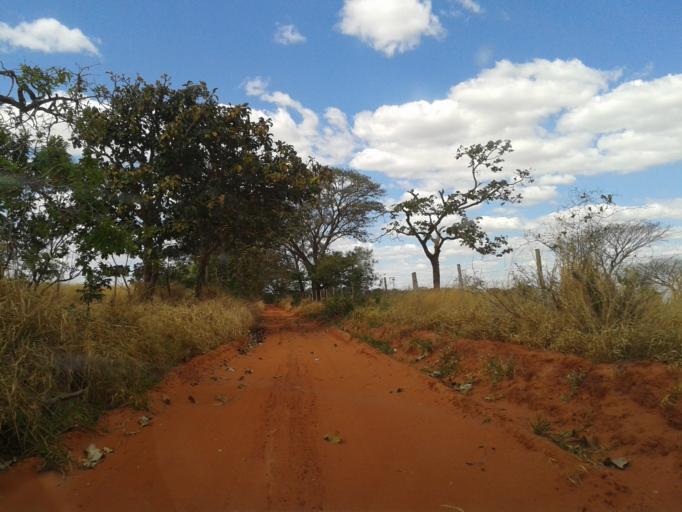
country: BR
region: Minas Gerais
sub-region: Monte Alegre De Minas
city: Monte Alegre de Minas
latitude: -18.7766
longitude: -49.0818
